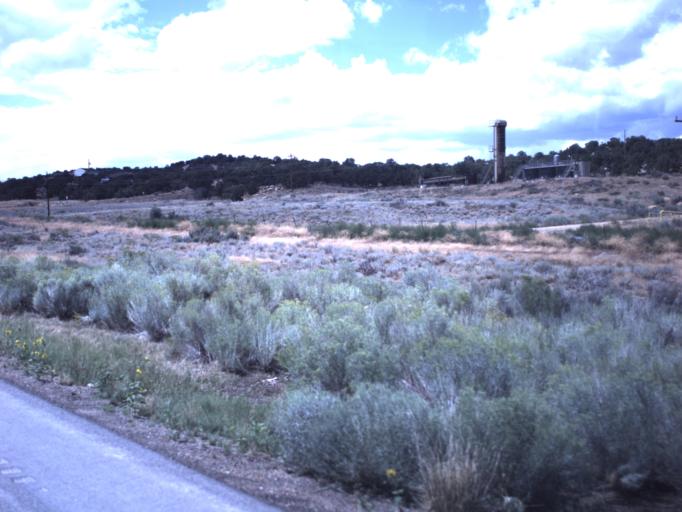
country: US
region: Utah
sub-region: Duchesne County
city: Duchesne
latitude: 40.1714
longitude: -110.5731
